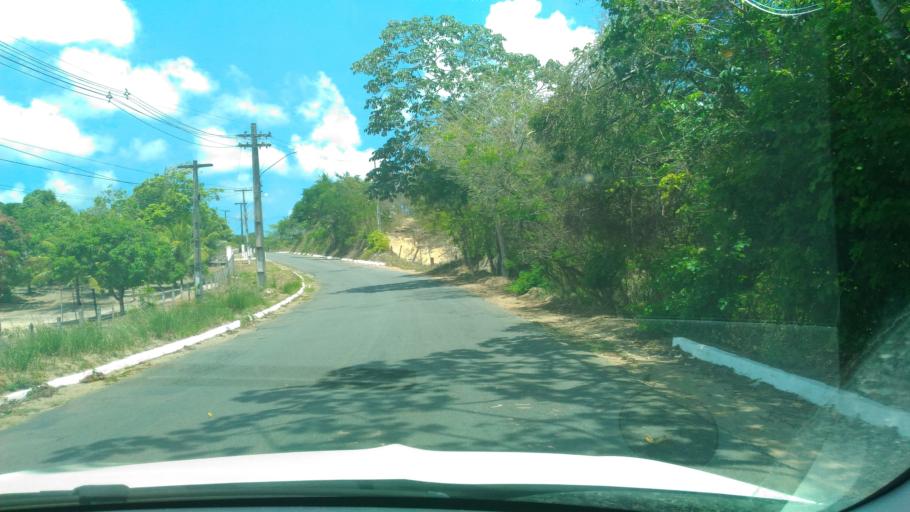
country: BR
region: Paraiba
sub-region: Conde
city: Conde
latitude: -7.2630
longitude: -34.9233
